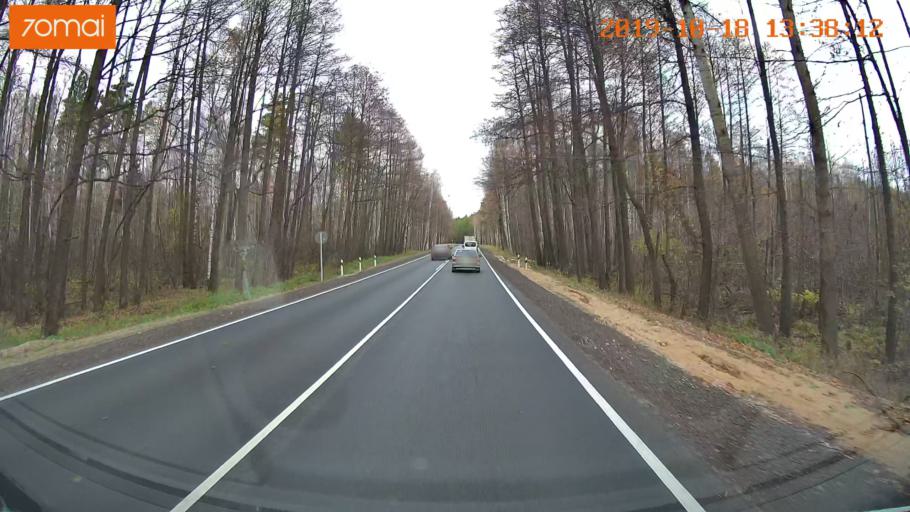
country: RU
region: Rjazan
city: Solotcha
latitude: 54.8874
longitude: 40.0015
